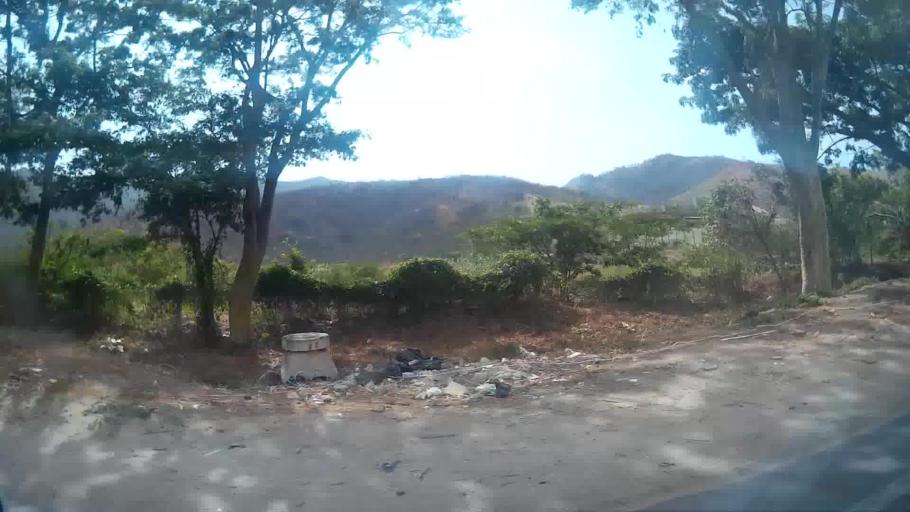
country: CO
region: Magdalena
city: Santa Marta
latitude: 11.2046
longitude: -74.1961
